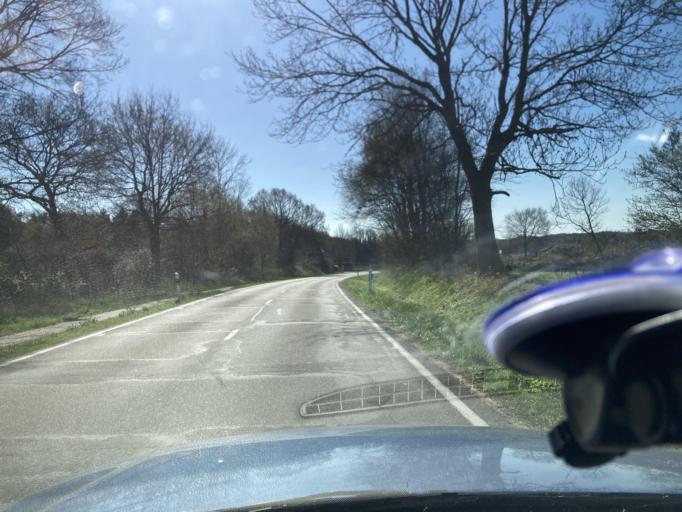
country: DE
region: Schleswig-Holstein
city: Nordhastedt
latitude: 54.1698
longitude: 9.1908
